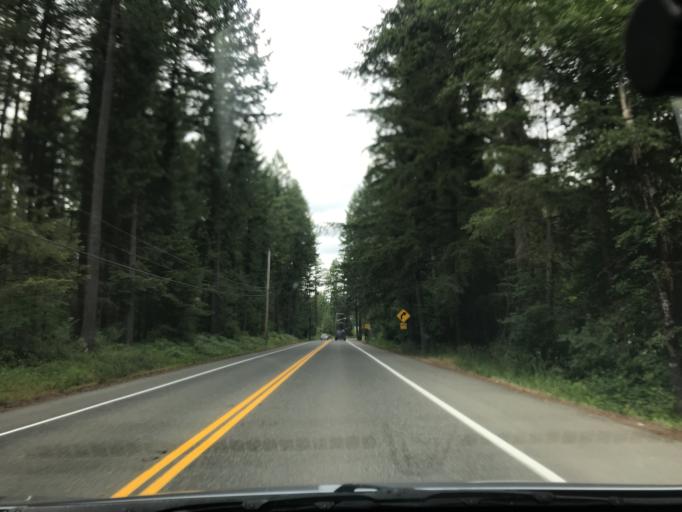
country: US
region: Washington
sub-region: King County
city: Black Diamond
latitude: 47.3058
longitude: -122.0481
